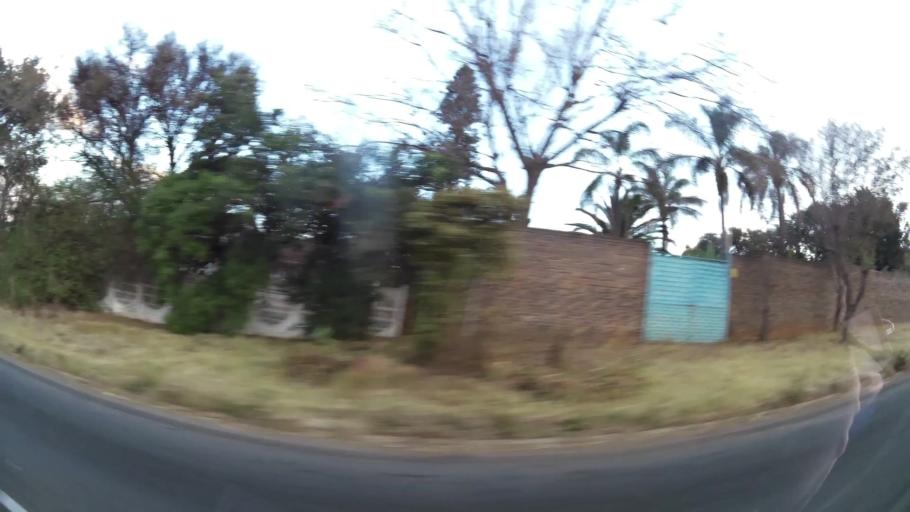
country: ZA
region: Gauteng
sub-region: West Rand District Municipality
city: Krugersdorp
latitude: -26.0760
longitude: 27.7872
